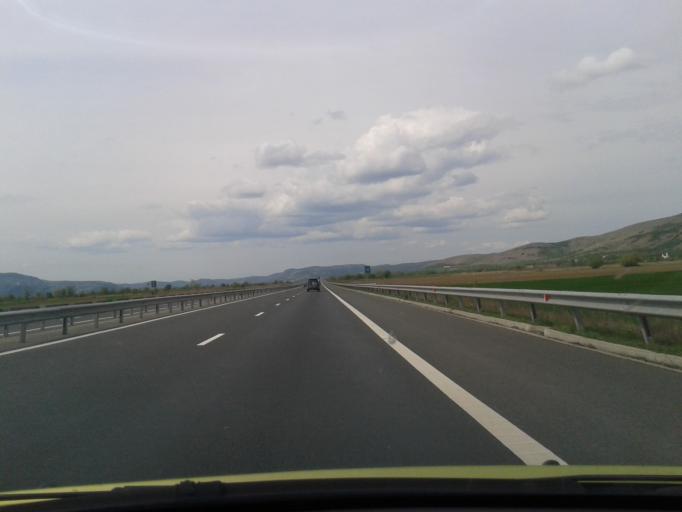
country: RO
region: Hunedoara
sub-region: Oras Simeria
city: Simeria
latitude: 45.8751
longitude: 23.0065
